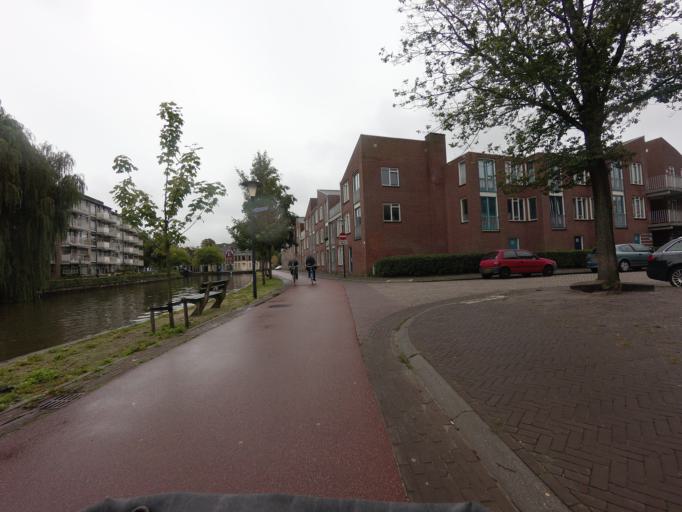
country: NL
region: Friesland
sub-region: Gemeente Leeuwarden
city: Bilgaard
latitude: 53.2081
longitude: 5.7979
